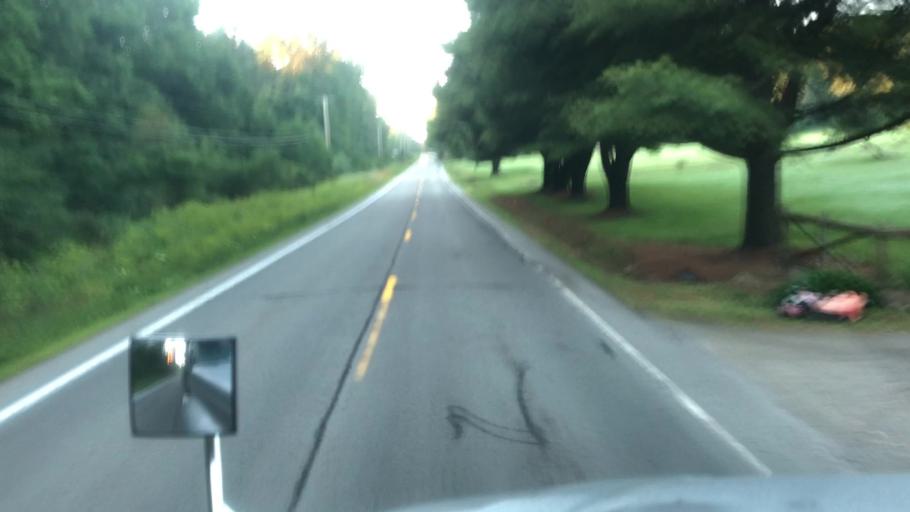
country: US
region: Pennsylvania
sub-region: Crawford County
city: Titusville
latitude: 41.5860
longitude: -79.6098
